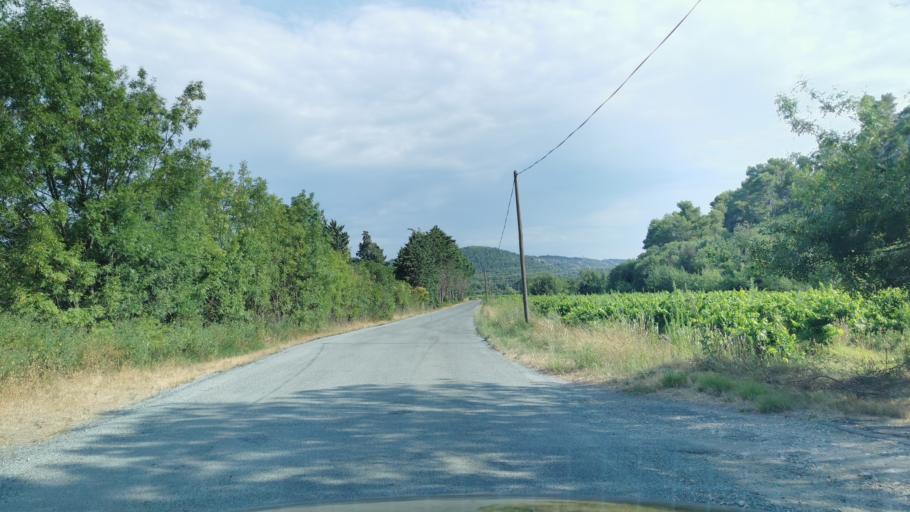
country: FR
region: Languedoc-Roussillon
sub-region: Departement de l'Aude
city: Bize-Minervois
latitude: 43.3344
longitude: 2.8766
